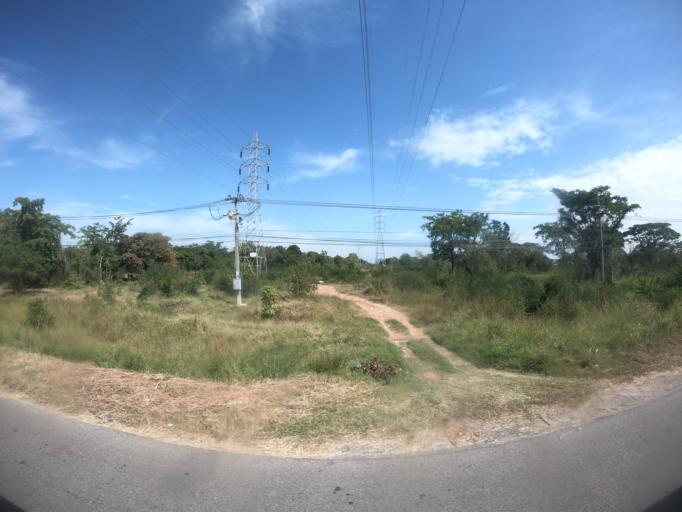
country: TH
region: Khon Kaen
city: Khon Kaen
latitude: 16.3911
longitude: 102.8066
